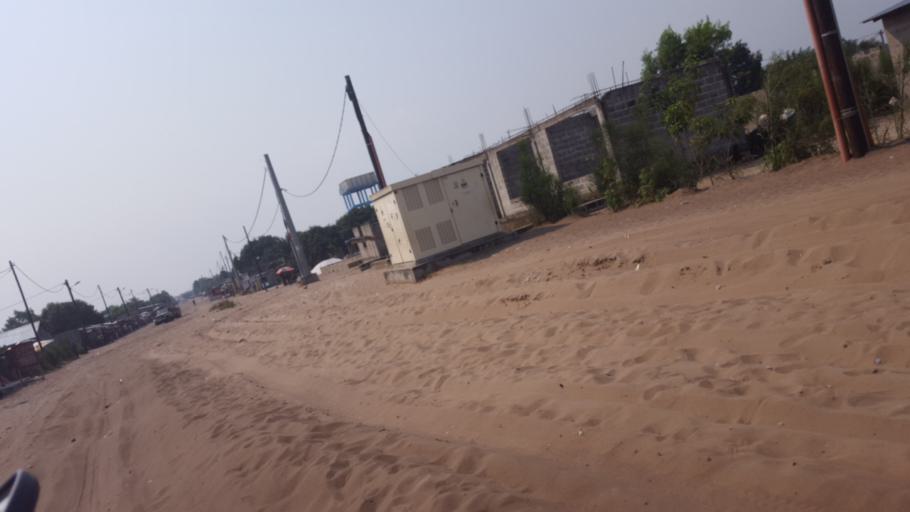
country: CD
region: Kinshasa
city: Masina
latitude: -4.3687
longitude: 15.5148
